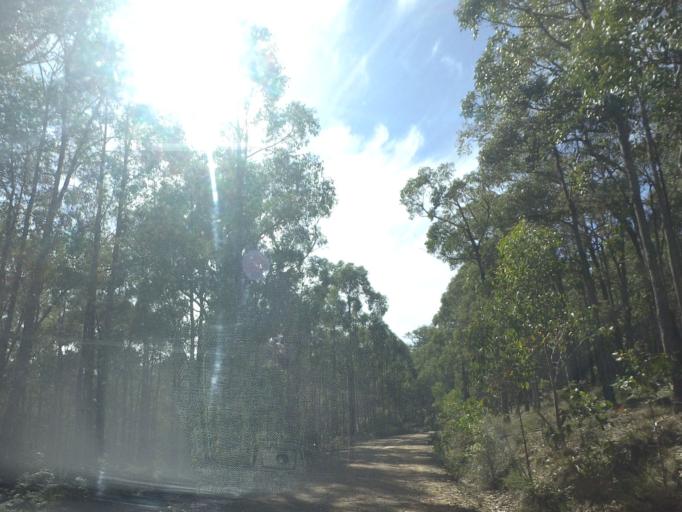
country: AU
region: Victoria
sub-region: Moorabool
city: Bacchus Marsh
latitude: -37.4424
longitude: 144.2693
